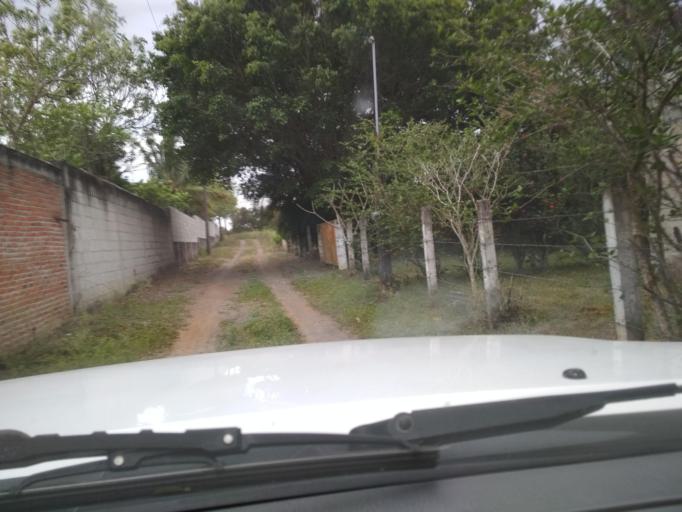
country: MX
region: Veracruz
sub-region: Veracruz
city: Delfino Victoria (Santa Fe)
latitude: 19.1730
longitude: -96.2784
